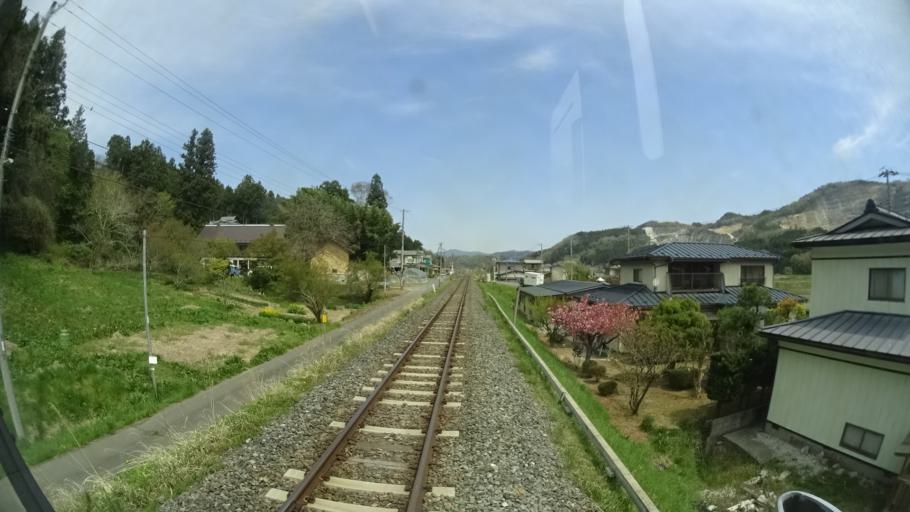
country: JP
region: Iwate
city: Ichinoseki
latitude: 38.9655
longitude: 141.2397
